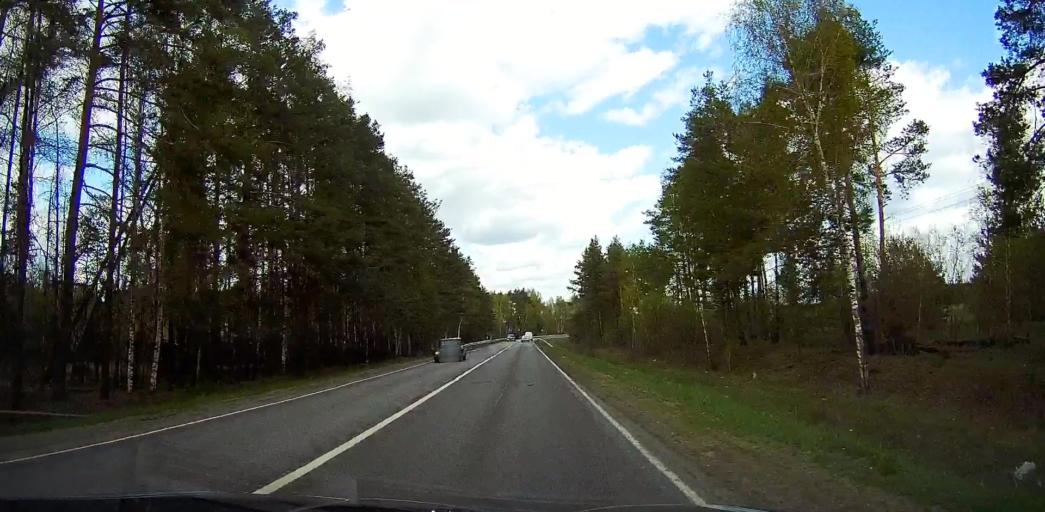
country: RU
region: Moskovskaya
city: Davydovo
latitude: 55.6280
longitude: 38.8619
